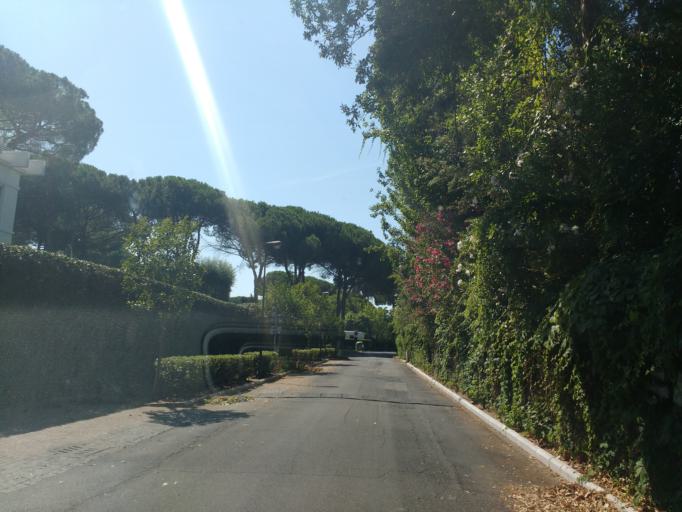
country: IT
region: Latium
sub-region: Citta metropolitana di Roma Capitale
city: Acilia-Castel Fusano-Ostia Antica
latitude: 41.7508
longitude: 12.3585
